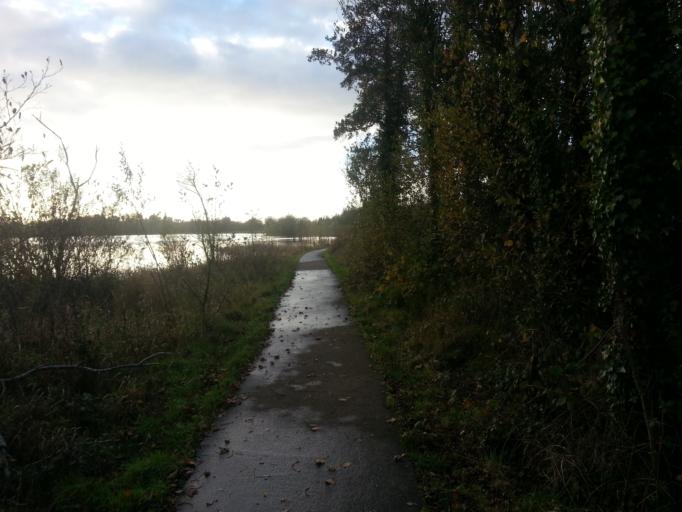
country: IE
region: Ulster
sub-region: County Monaghan
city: Clones
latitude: 54.2299
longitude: -7.2831
